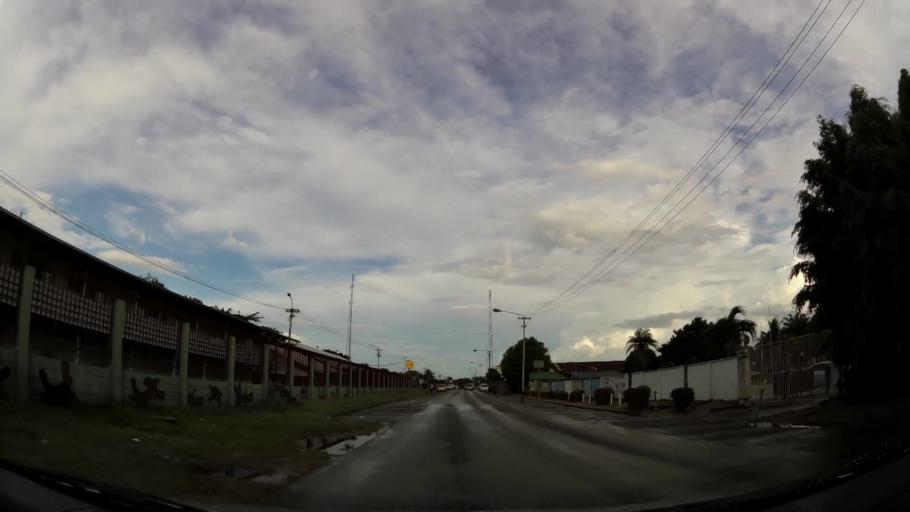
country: SR
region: Paramaribo
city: Paramaribo
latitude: 5.8265
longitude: -55.1802
